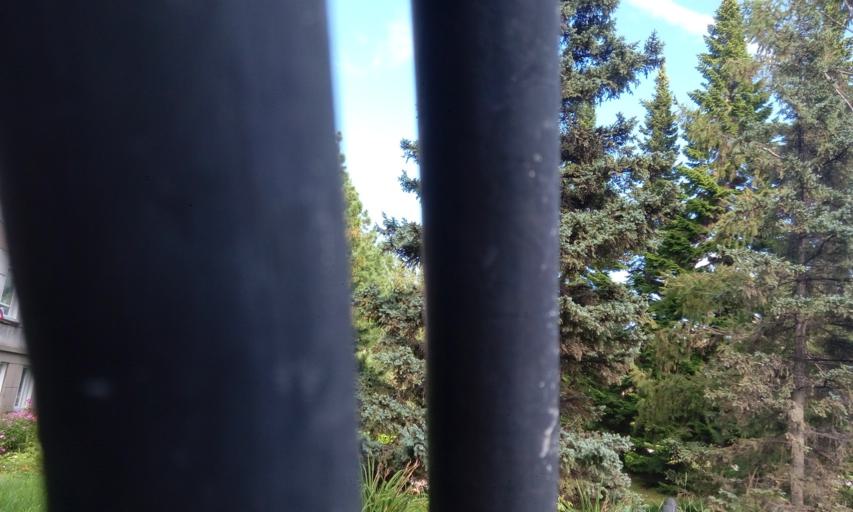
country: RU
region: Novosibirsk
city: Akademgorodok
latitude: 54.8474
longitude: 83.1069
